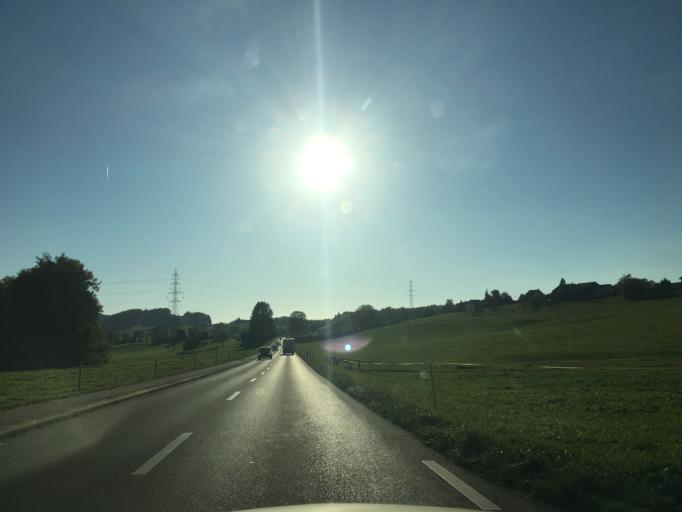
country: CH
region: Vaud
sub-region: Lavaux-Oron District
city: Savigny
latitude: 46.5391
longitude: 6.7665
